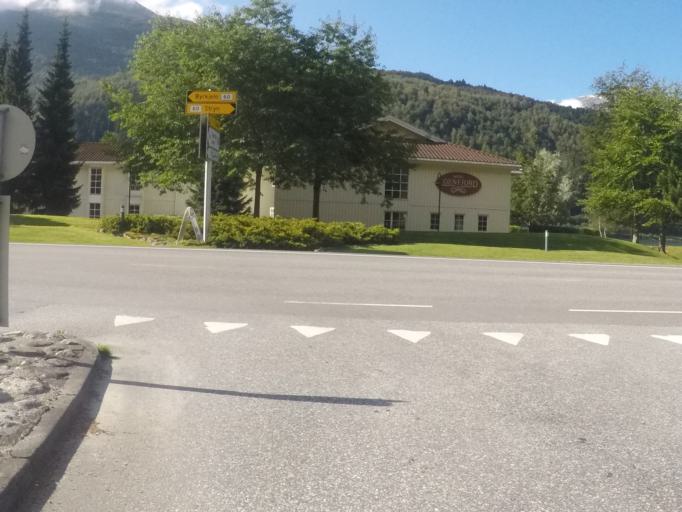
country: NO
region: Sogn og Fjordane
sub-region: Stryn
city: Stryn
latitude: 61.8715
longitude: 6.8459
